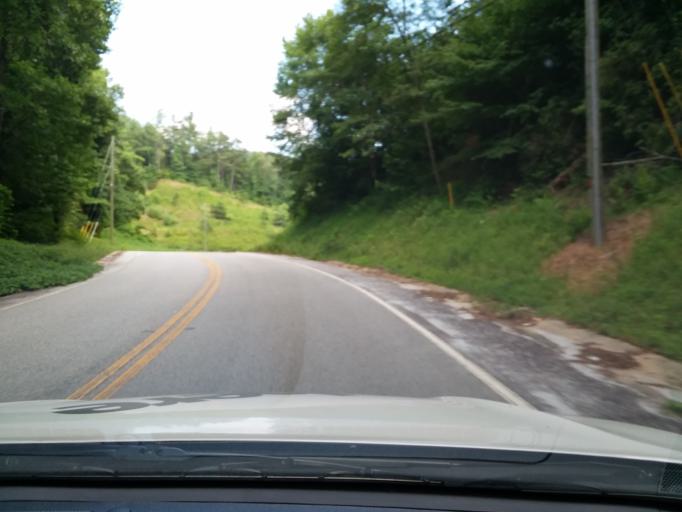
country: US
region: Georgia
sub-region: Rabun County
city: Clayton
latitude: 34.7602
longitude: -83.3986
